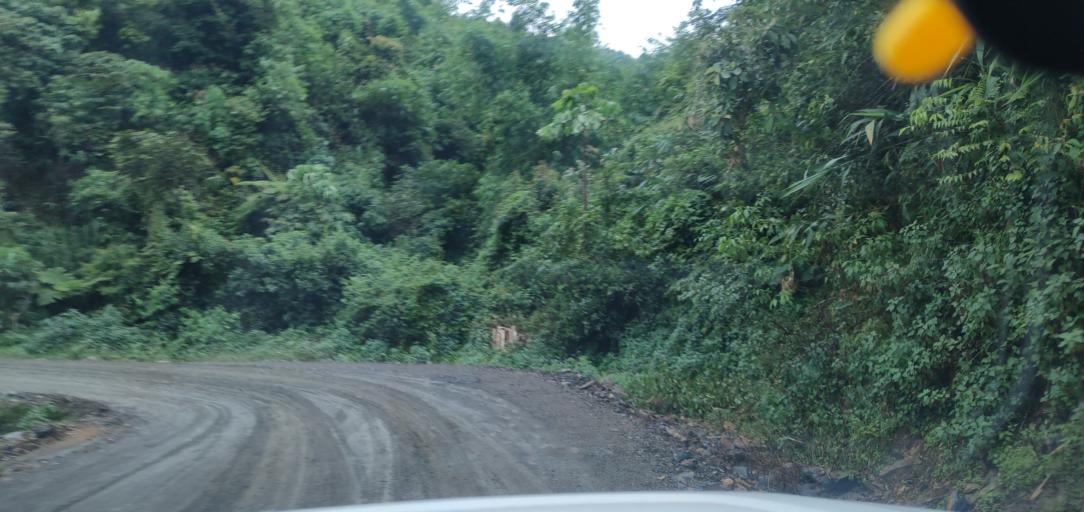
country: LA
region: Phongsali
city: Phongsali
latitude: 21.4286
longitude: 102.1641
